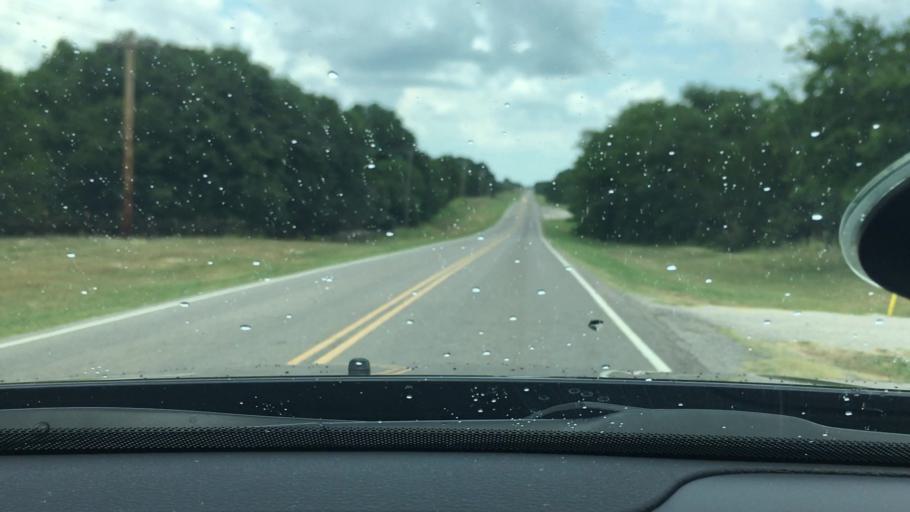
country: US
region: Oklahoma
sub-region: Love County
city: Marietta
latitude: 33.9444
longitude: -97.0367
